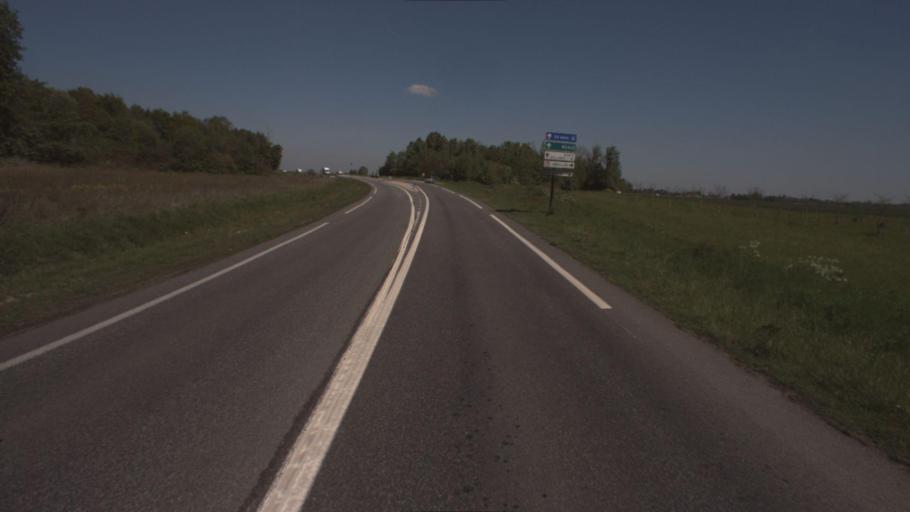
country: FR
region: Ile-de-France
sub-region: Departement de Seine-et-Marne
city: Voulangis
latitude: 48.8312
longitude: 2.8794
